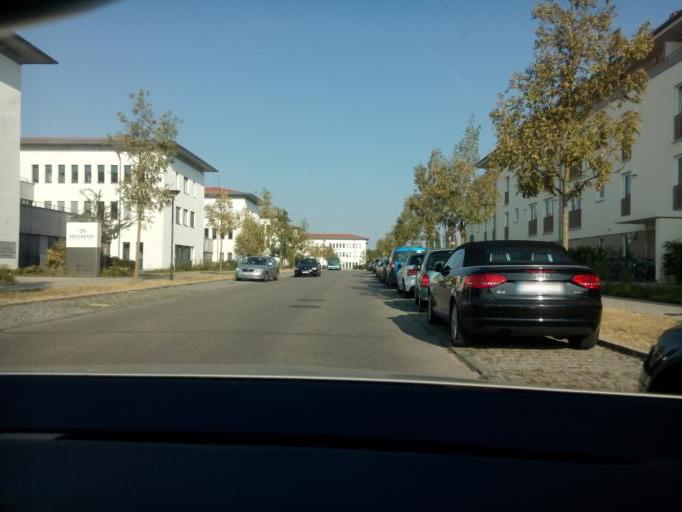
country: DE
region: Bavaria
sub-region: Upper Bavaria
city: Neubiberg
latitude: 48.0835
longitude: 11.6348
